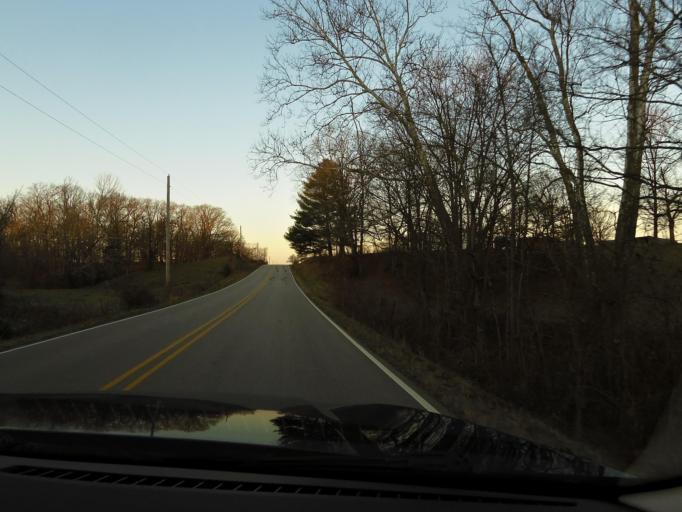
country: US
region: Illinois
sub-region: Marion County
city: Salem
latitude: 38.7588
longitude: -88.9015
